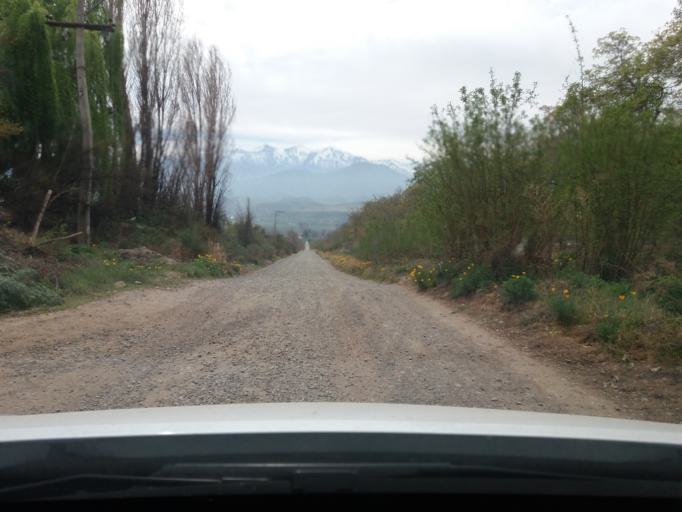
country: CL
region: Valparaiso
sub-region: Provincia de Los Andes
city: Los Andes
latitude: -32.8467
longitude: -70.5543
